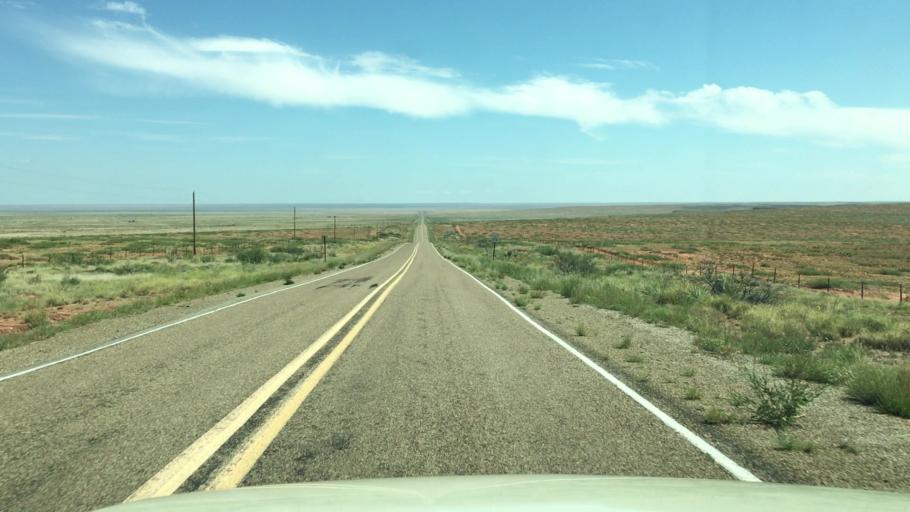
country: US
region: New Mexico
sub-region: Chaves County
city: Roswell
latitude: 33.9686
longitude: -104.5803
